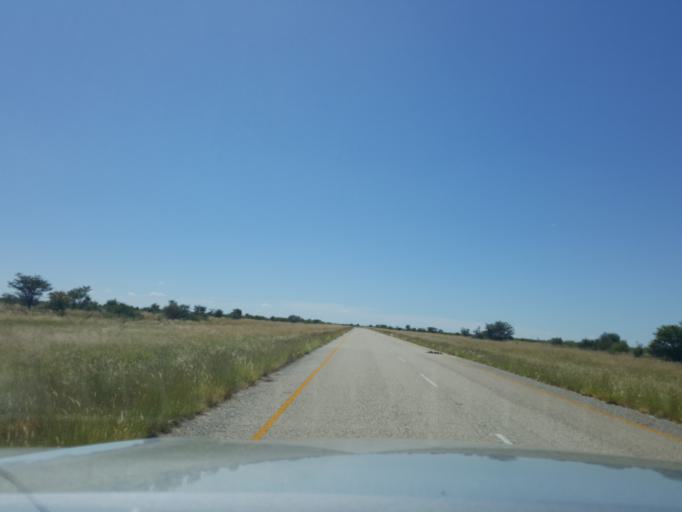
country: BW
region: Central
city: Gweta
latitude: -20.2309
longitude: 24.9648
